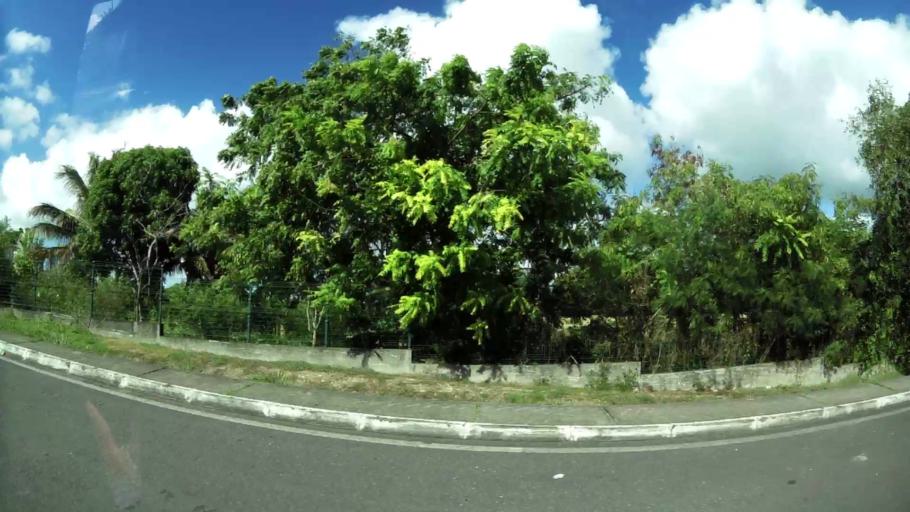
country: GP
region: Guadeloupe
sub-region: Guadeloupe
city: Sainte-Anne
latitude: 16.2486
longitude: -61.3612
